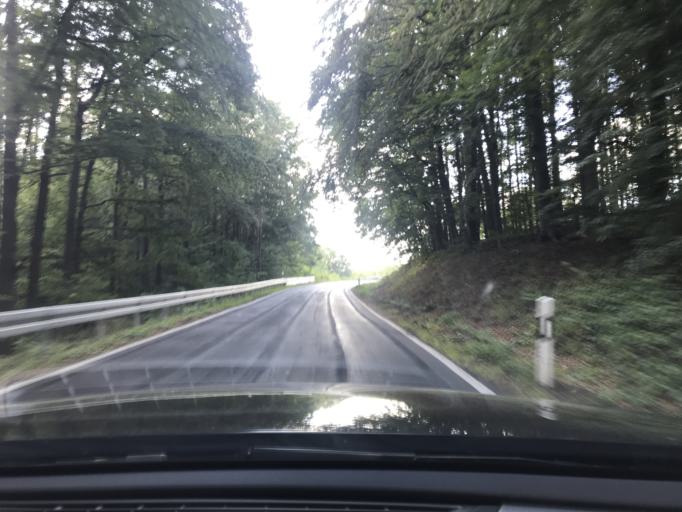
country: DE
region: Bavaria
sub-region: Regierungsbezirk Unterfranken
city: Kirchlauter
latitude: 50.0724
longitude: 10.6641
